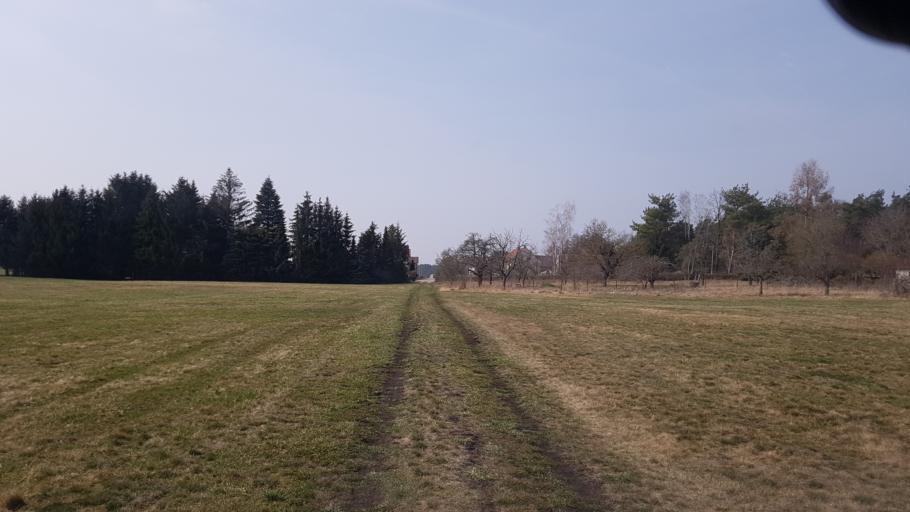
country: DE
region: Brandenburg
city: Schilda
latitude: 51.6096
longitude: 13.3931
